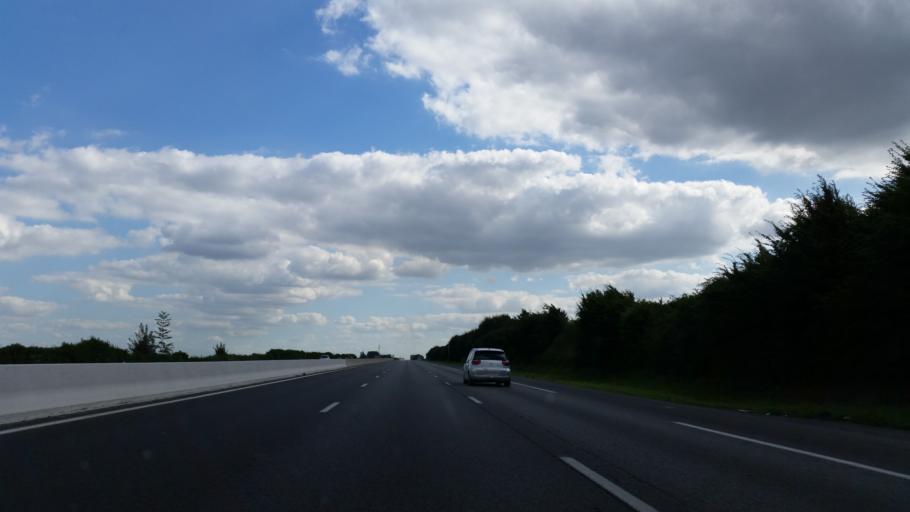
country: FR
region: Nord-Pas-de-Calais
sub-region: Departement du Pas-de-Calais
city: Bapaume
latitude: 50.1205
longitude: 2.8716
